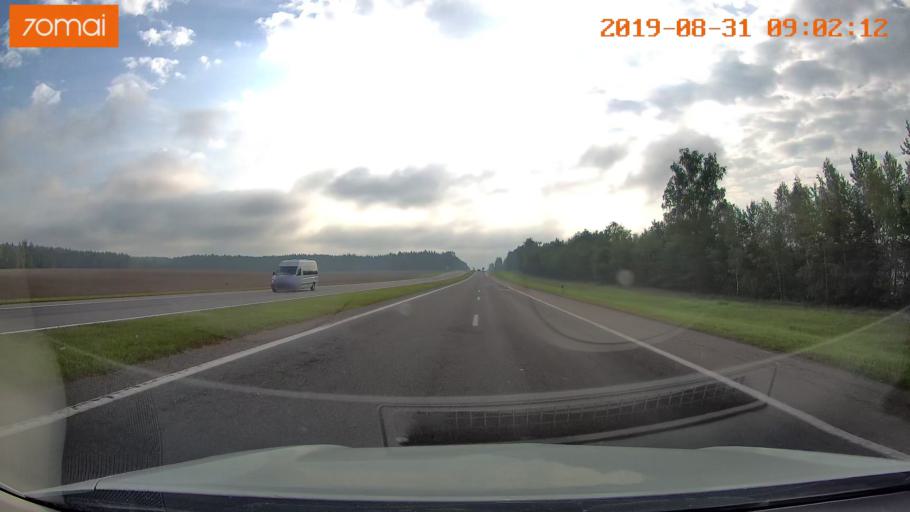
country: BY
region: Minsk
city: Chervyen'
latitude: 53.7462
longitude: 28.2817
